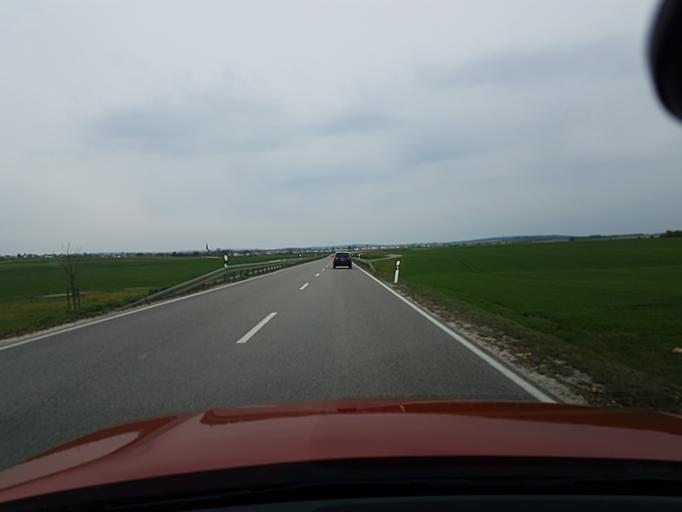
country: DE
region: Bavaria
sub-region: Upper Bavaria
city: Gaimersheim
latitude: 48.8258
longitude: 11.3454
